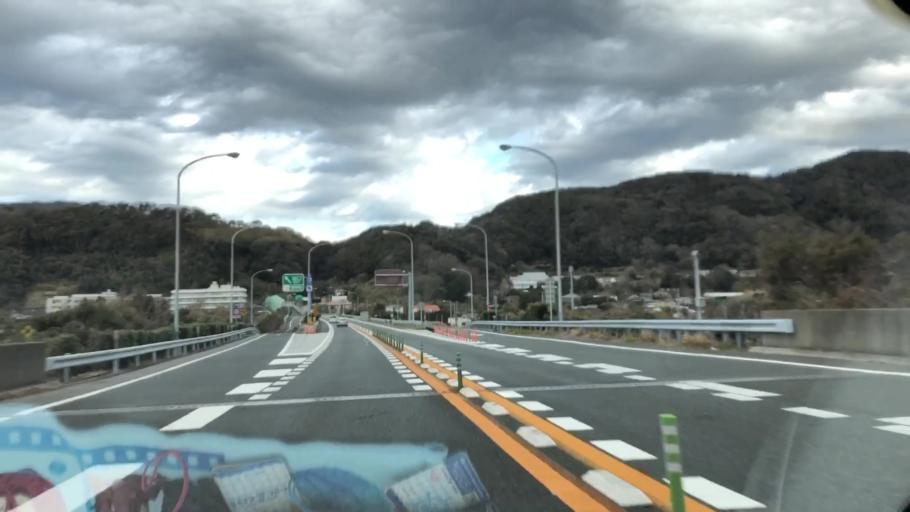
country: JP
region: Chiba
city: Tateyama
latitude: 35.1406
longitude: 139.8477
